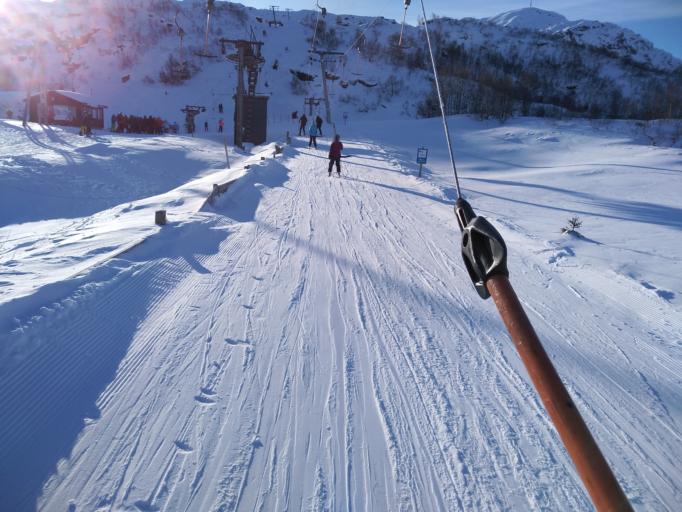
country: NO
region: Rogaland
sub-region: Sauda
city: Sauda
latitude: 59.6192
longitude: 6.2347
